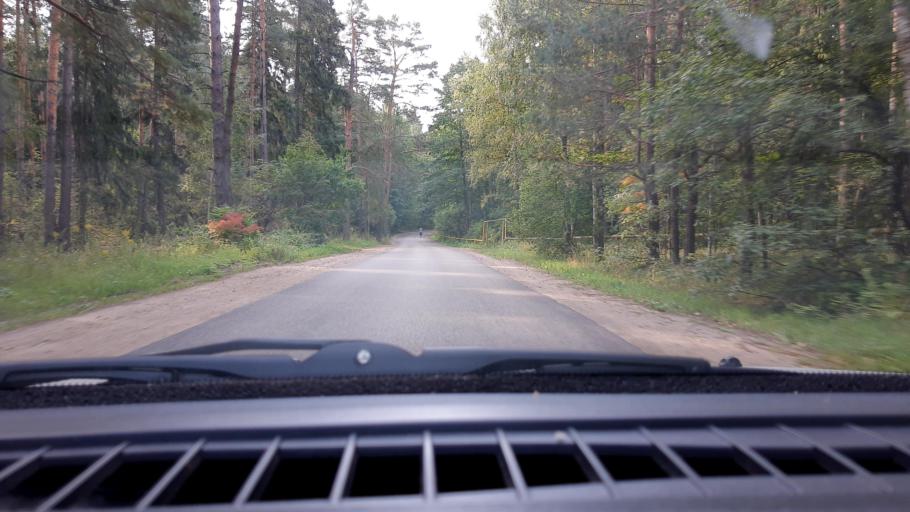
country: RU
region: Nizjnij Novgorod
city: Afonino
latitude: 56.1820
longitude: 44.0799
